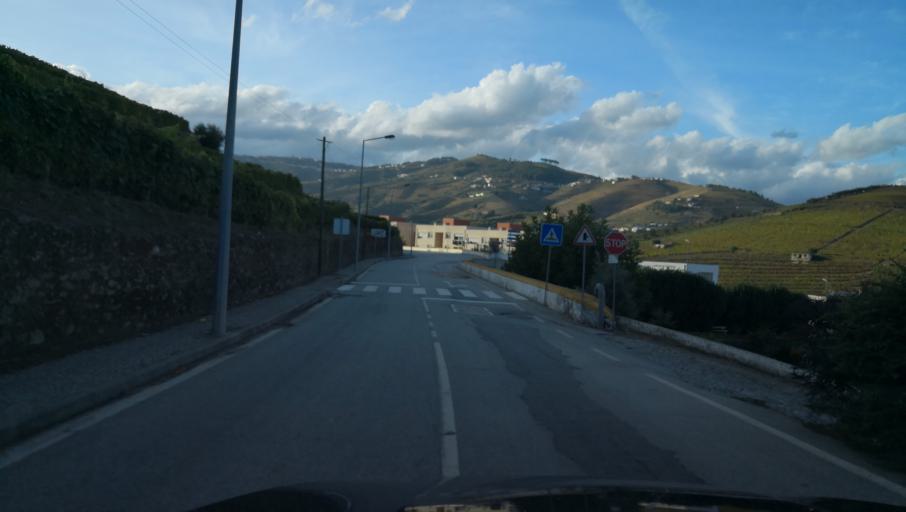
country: PT
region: Vila Real
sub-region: Santa Marta de Penaguiao
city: Santa Marta de Penaguiao
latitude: 41.2075
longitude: -7.7793
